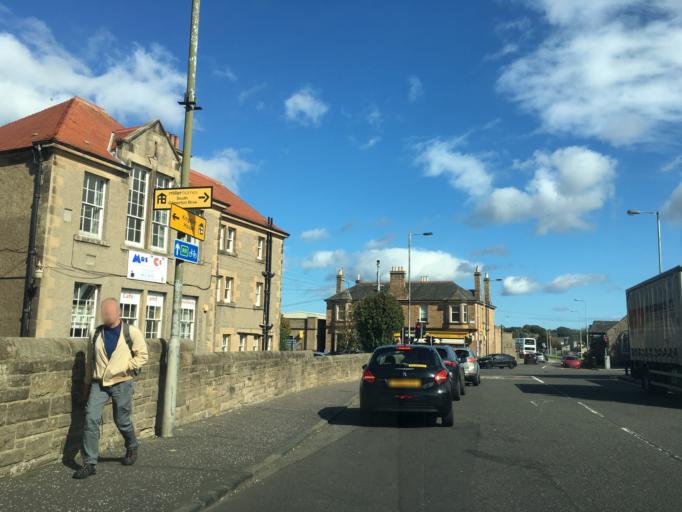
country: GB
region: Scotland
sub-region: Midlothian
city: Loanhead
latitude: 55.9057
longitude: -3.1341
